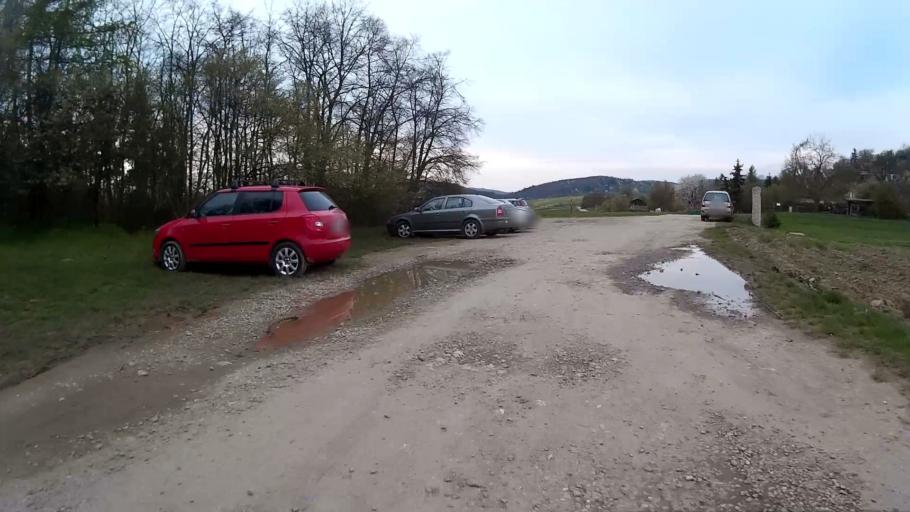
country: CZ
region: South Moravian
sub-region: Mesto Brno
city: Mokra Hora
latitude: 49.2296
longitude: 16.5498
